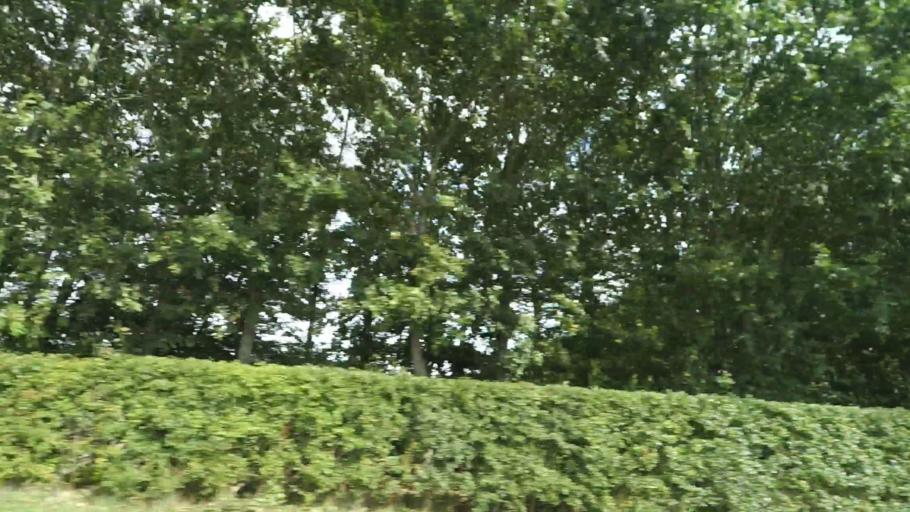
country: DK
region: Central Jutland
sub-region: Norddjurs Kommune
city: Auning
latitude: 56.4833
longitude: 10.4554
